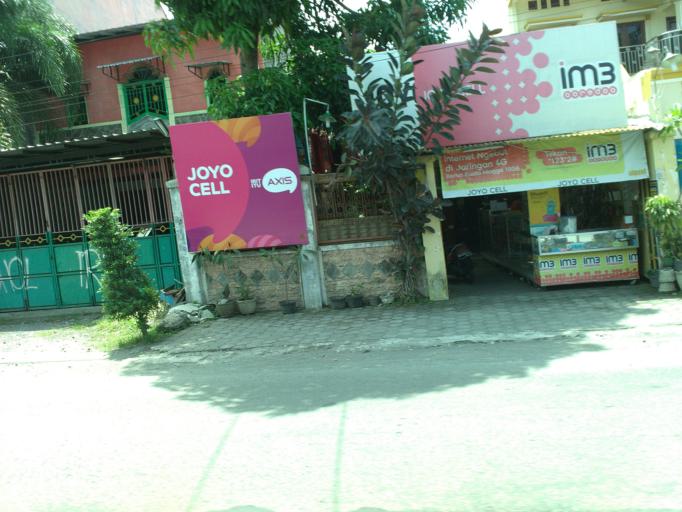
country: ID
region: Central Java
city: Klaten
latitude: -7.6893
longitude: 110.6107
